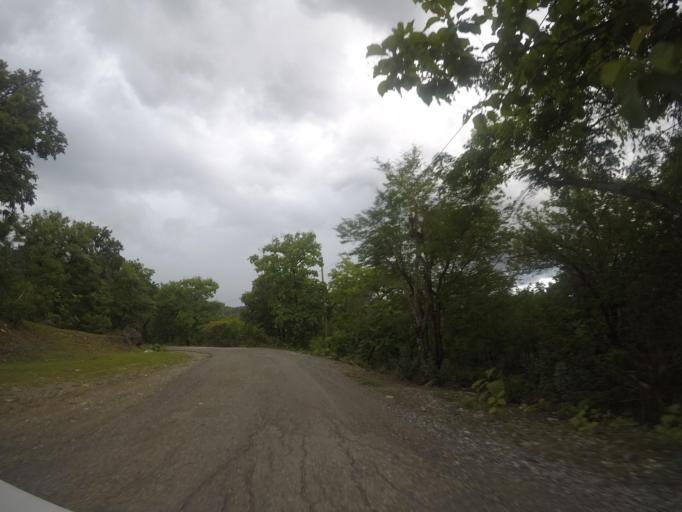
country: ID
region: East Nusa Tenggara
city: Atambua
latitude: -8.9669
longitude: 125.0224
